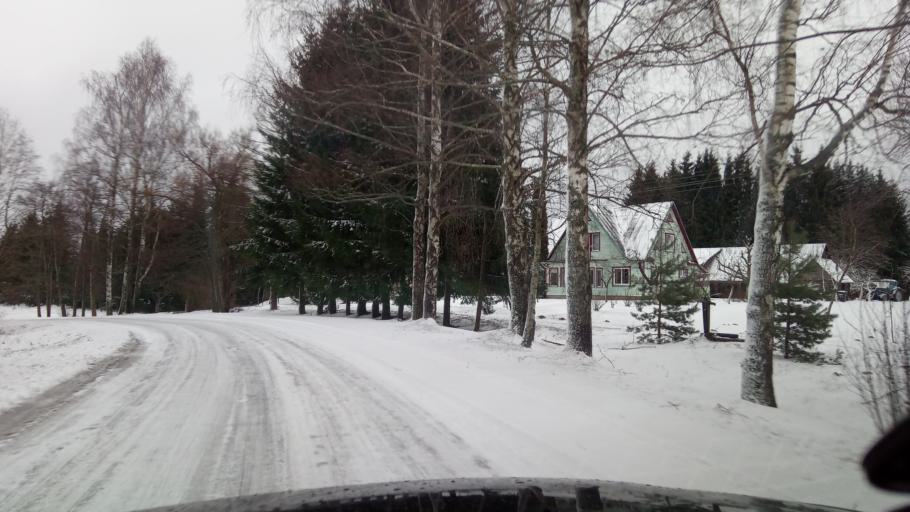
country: LT
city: Zarasai
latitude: 55.6250
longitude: 25.9566
